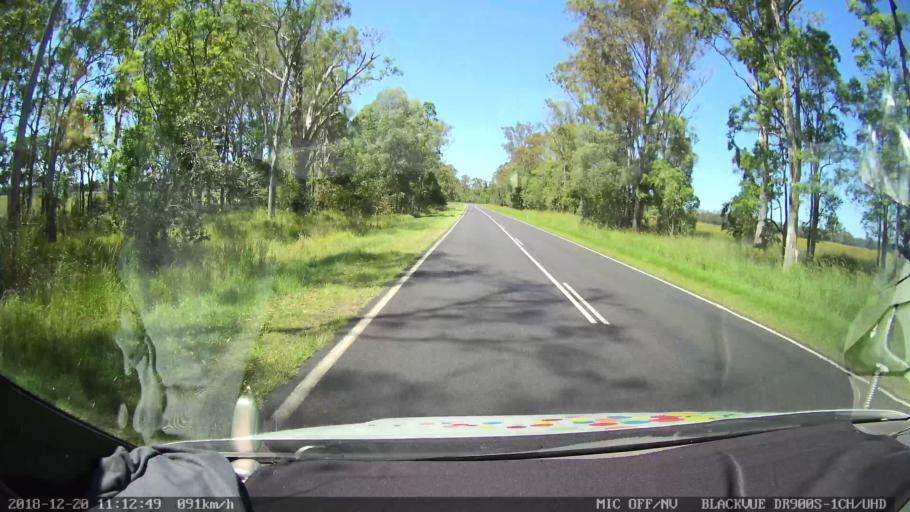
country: AU
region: New South Wales
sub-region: Richmond Valley
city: Casino
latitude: -28.9793
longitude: 153.0098
